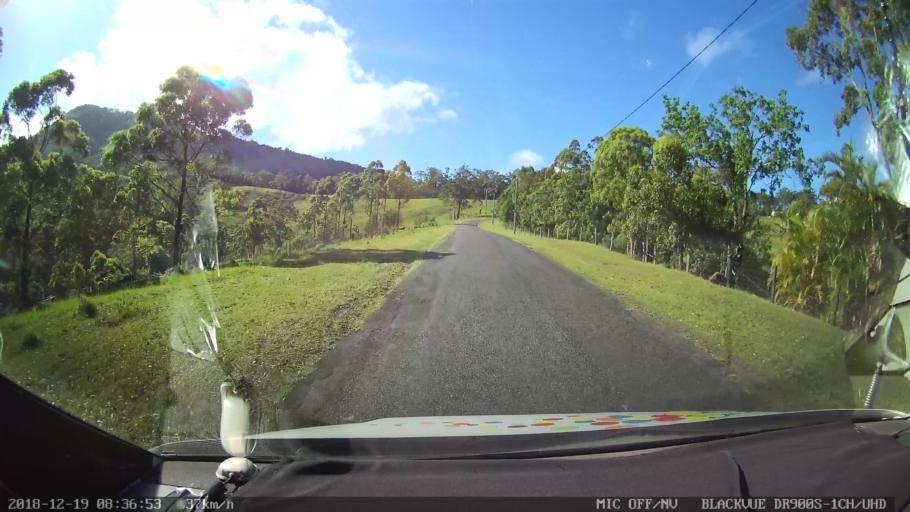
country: AU
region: New South Wales
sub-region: Kyogle
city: Kyogle
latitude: -28.3286
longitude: 152.9733
